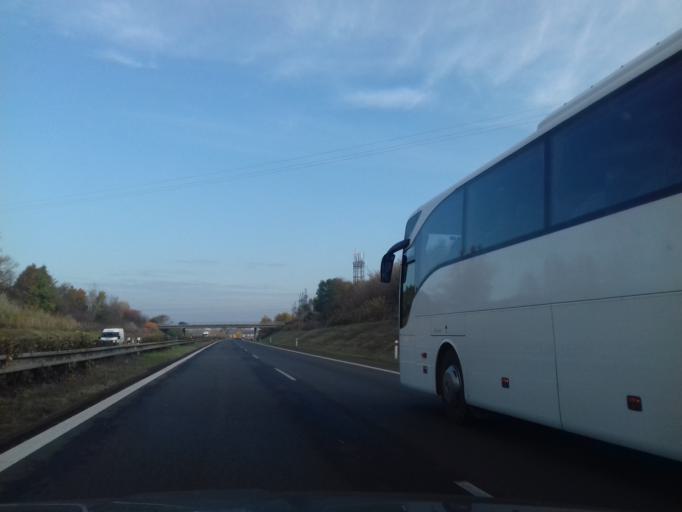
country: SK
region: Bratislavsky
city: Stupava
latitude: 48.2845
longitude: 17.0097
